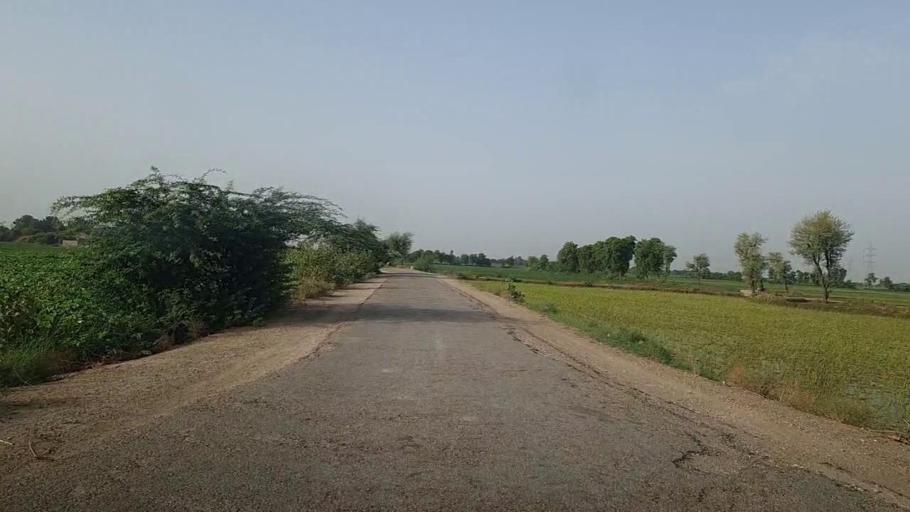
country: PK
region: Sindh
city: Mehar
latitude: 27.1367
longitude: 67.7902
